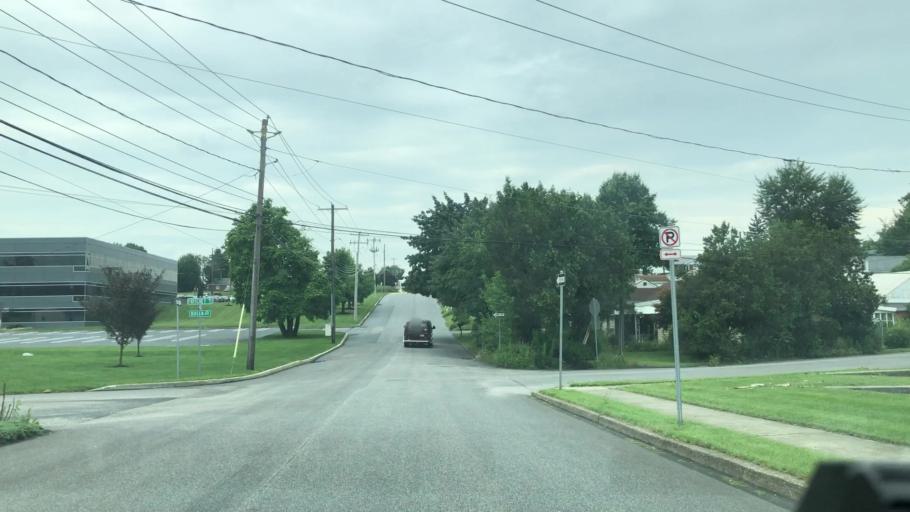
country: US
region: Pennsylvania
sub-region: Dauphin County
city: Colonial Park
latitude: 40.3021
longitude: -76.8110
